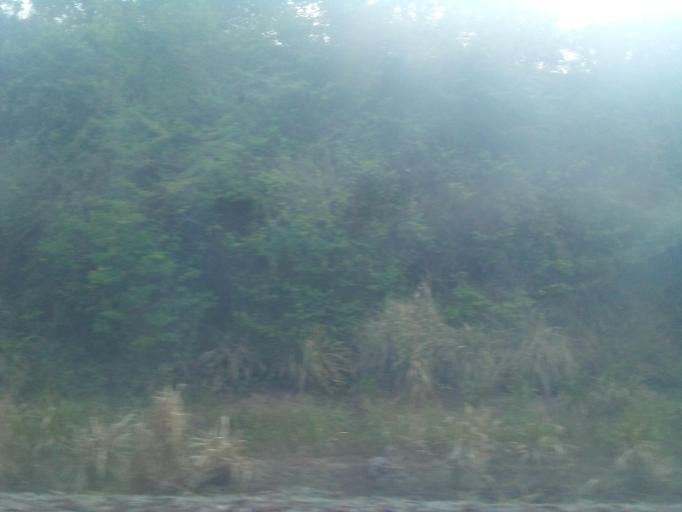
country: BR
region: Maranhao
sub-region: Sao Luis
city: Sao Luis
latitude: -2.6436
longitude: -44.3050
